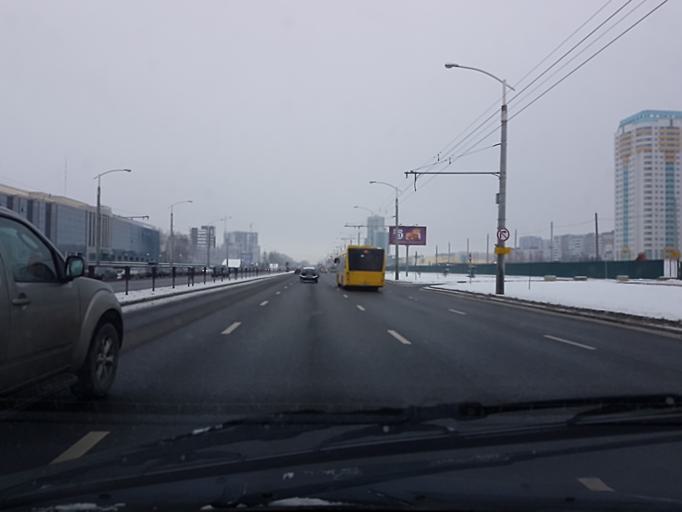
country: BY
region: Minsk
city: Novoye Medvezhino
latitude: 53.8668
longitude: 27.4885
